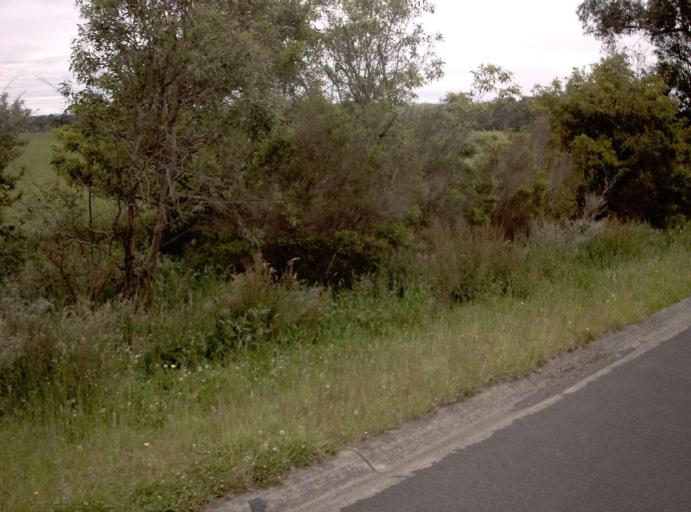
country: AU
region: Victoria
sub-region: Baw Baw
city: Warragul
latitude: -38.5867
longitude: 146.0608
